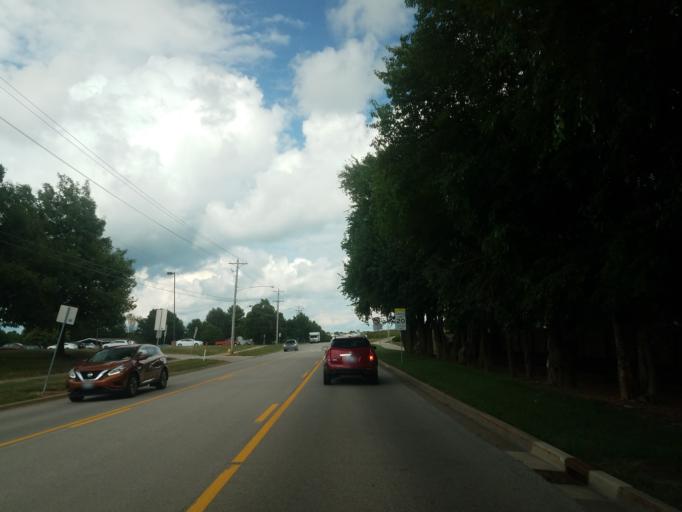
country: US
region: Illinois
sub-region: McLean County
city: Normal
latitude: 40.5103
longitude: -88.9346
